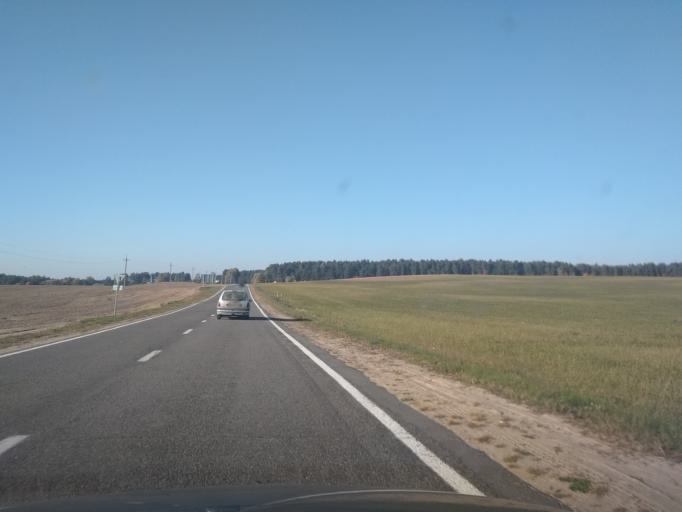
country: BY
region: Grodnenskaya
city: Vawkavysk
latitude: 53.1466
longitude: 24.5035
